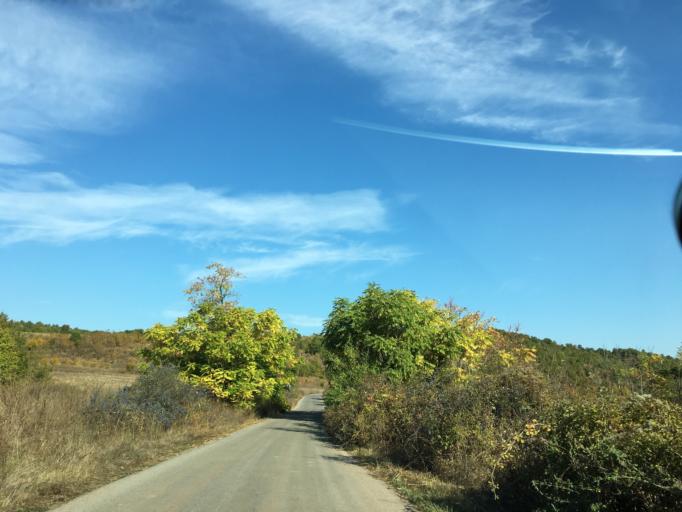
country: BG
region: Khaskovo
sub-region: Obshtina Ivaylovgrad
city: Ivaylovgrad
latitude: 41.4022
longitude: 26.1233
